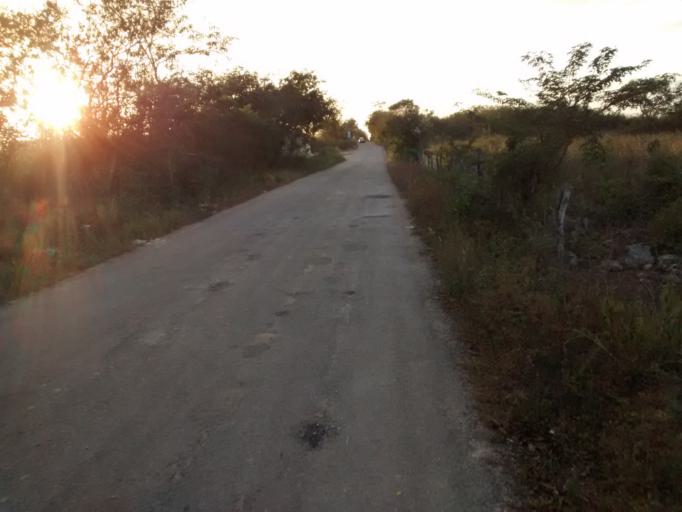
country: MX
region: Yucatan
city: Valladolid
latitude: 20.6829
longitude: -88.1714
